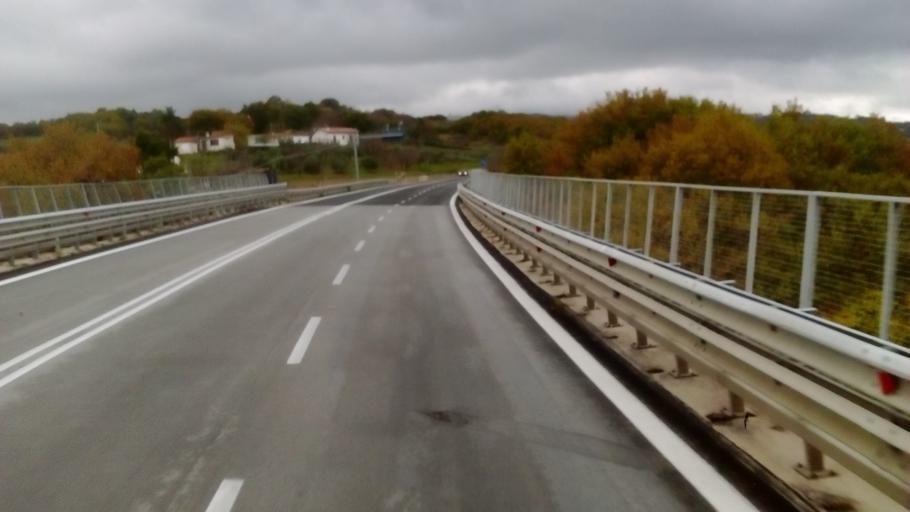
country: IT
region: Molise
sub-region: Provincia di Isernia
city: Bagnoli del Trigno
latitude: 41.7264
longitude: 14.4459
